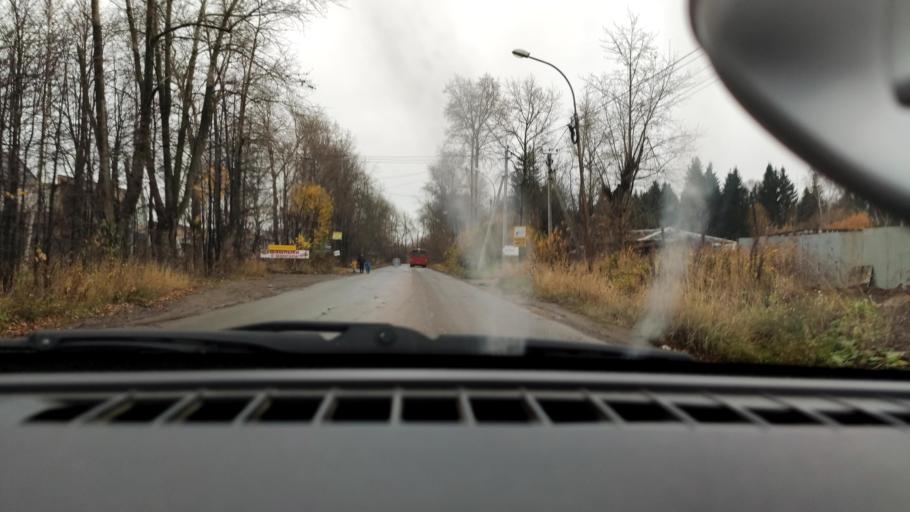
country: RU
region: Perm
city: Perm
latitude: 57.9598
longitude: 56.1963
